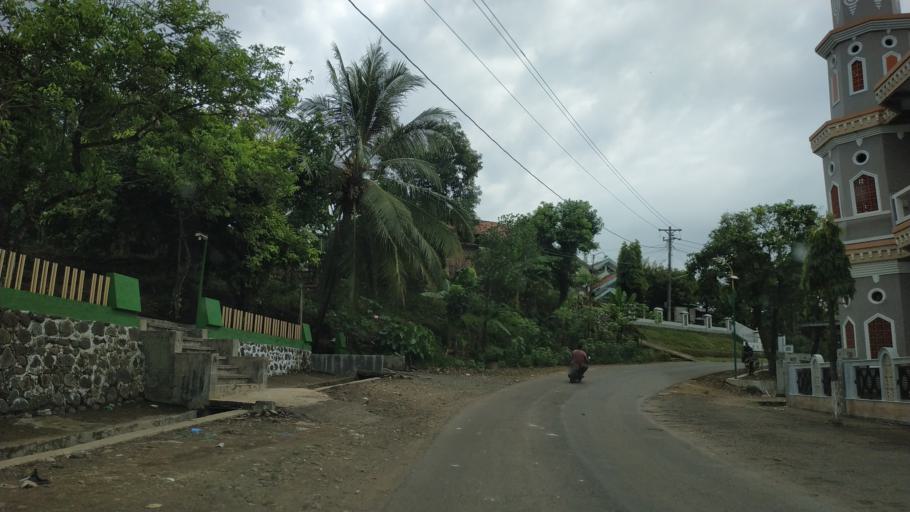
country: ID
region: Central Java
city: Krajan Tegalombo
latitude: -6.4453
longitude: 110.9851
